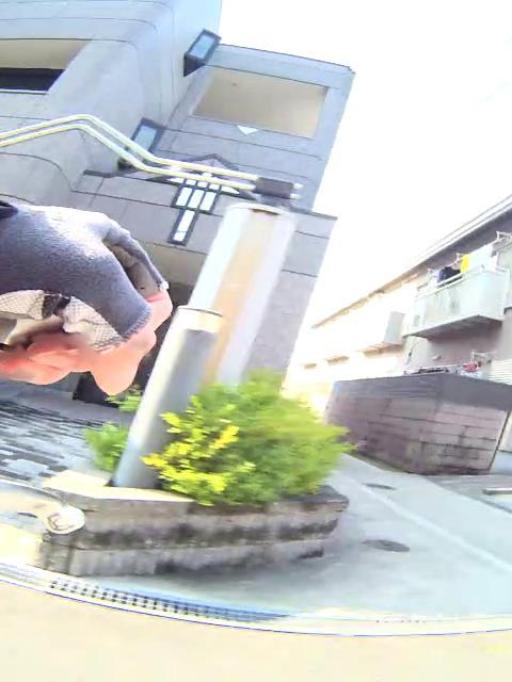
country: JP
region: Osaka
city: Suita
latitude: 34.7359
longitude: 135.4886
